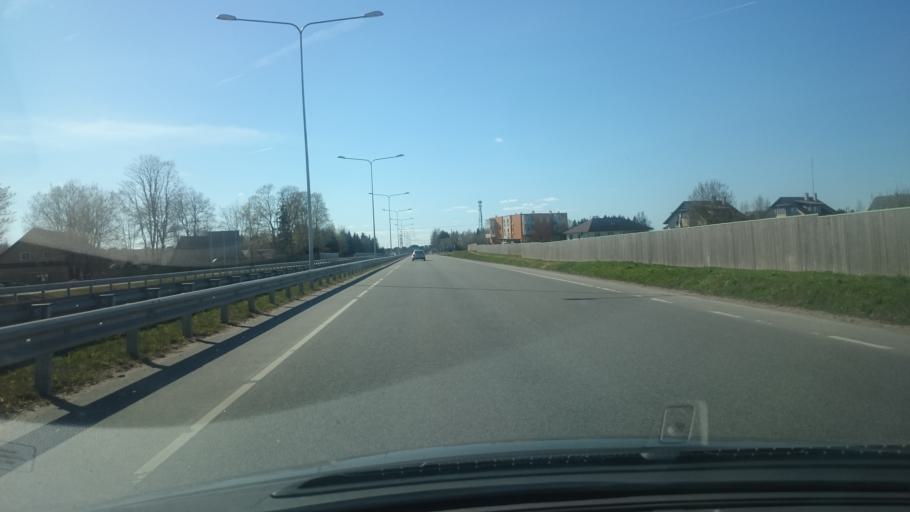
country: EE
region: Tartu
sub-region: Tartu linn
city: Tartu
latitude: 58.3733
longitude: 26.7956
